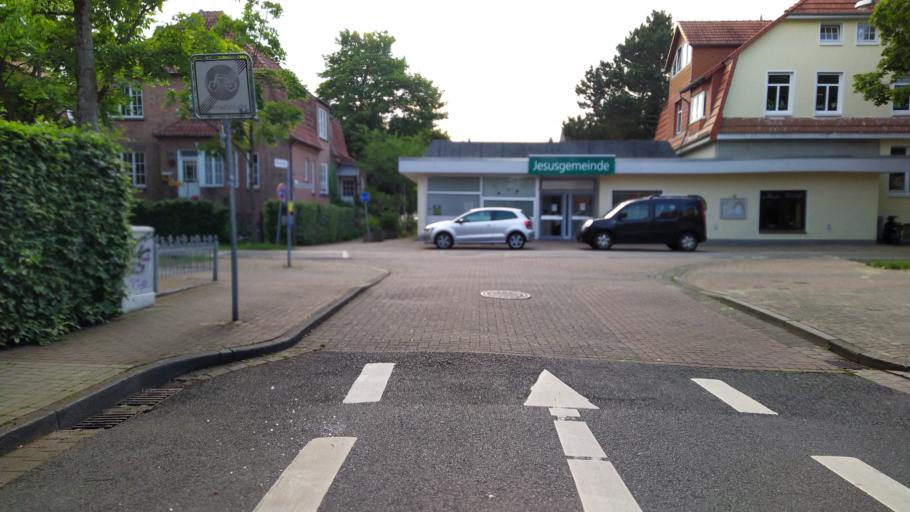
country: DE
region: Lower Saxony
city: Buxtehude
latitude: 53.4737
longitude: 9.6914
